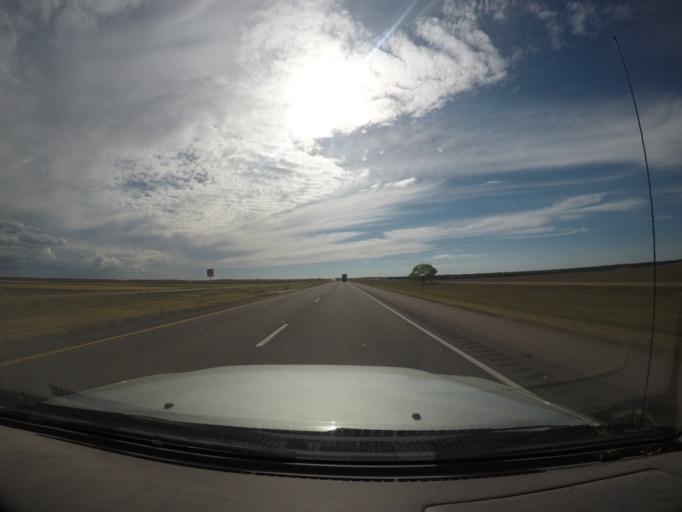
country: US
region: Nebraska
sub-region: Kimball County
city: Kimball
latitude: 41.1921
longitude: -103.8268
